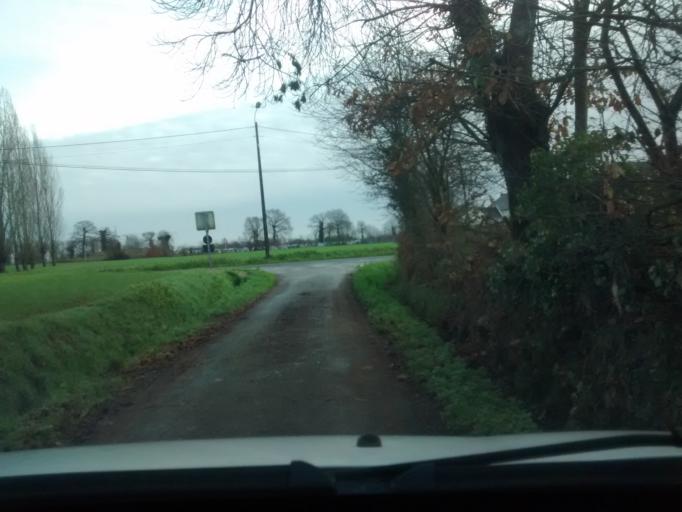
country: FR
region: Brittany
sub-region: Departement d'Ille-et-Vilaine
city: Montgermont
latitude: 48.1336
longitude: -1.7132
